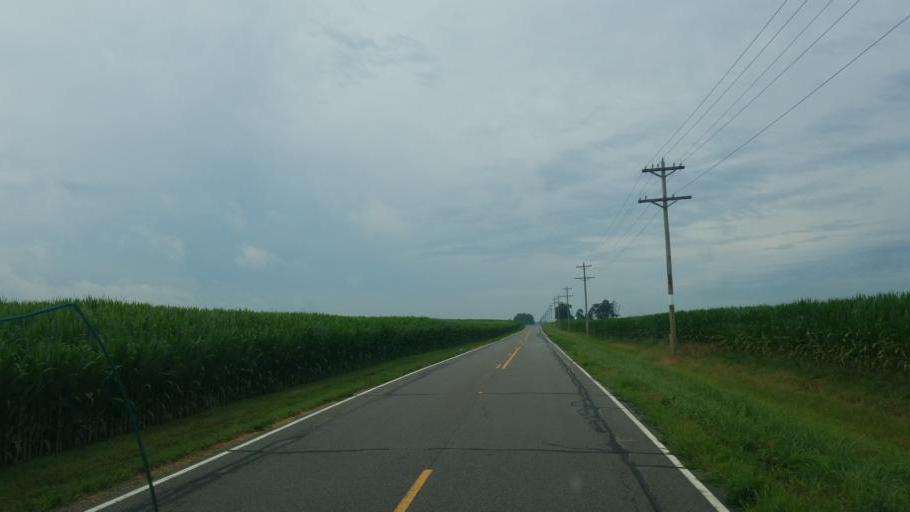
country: US
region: Ohio
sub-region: Defiance County
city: Hicksville
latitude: 41.3234
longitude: -84.6901
